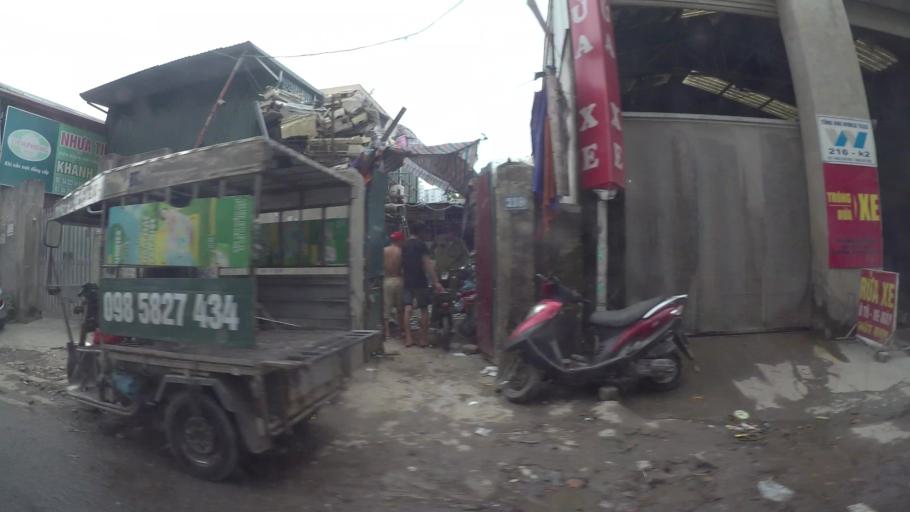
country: VN
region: Ha Noi
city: Cau Dien
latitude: 21.0320
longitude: 105.7594
